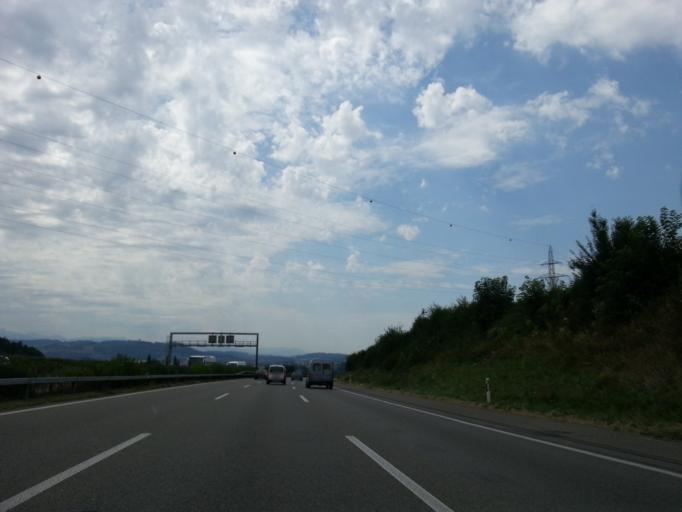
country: CH
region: Bern
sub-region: Bern-Mittelland District
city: Bolligen
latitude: 46.9935
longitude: 7.4829
